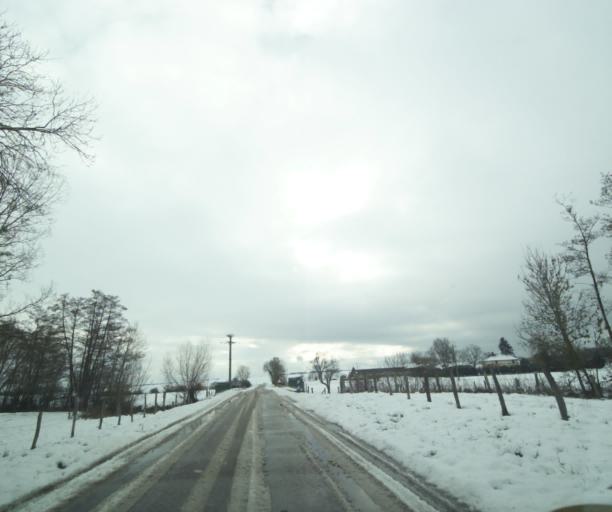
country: FR
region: Champagne-Ardenne
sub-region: Departement de la Haute-Marne
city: Montier-en-Der
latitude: 48.4519
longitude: 4.6954
